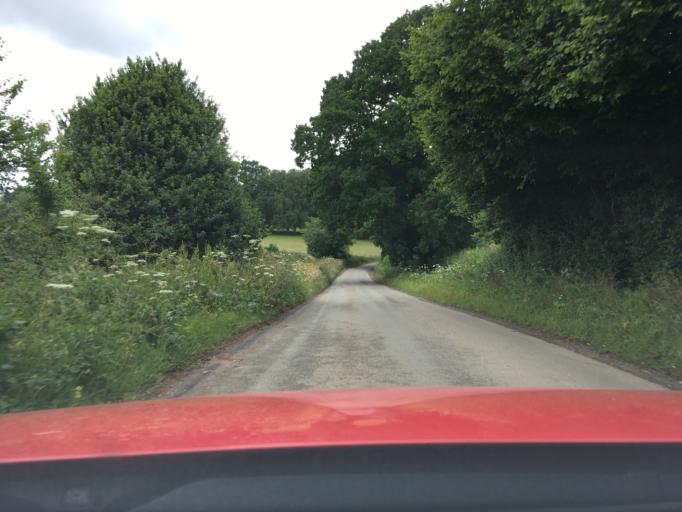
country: GB
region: England
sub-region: Gloucestershire
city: Mickleton
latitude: 52.0684
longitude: -1.7635
